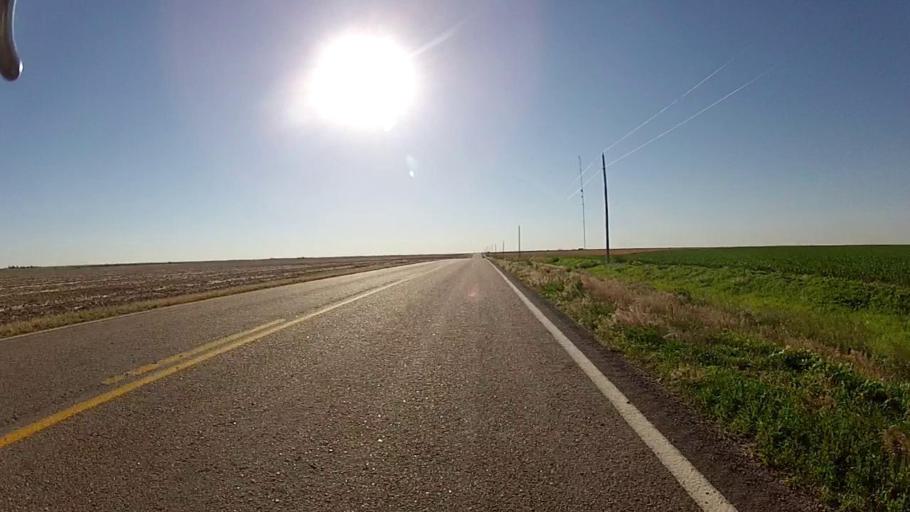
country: US
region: Kansas
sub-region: Ford County
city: Dodge City
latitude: 37.6464
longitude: -99.8470
